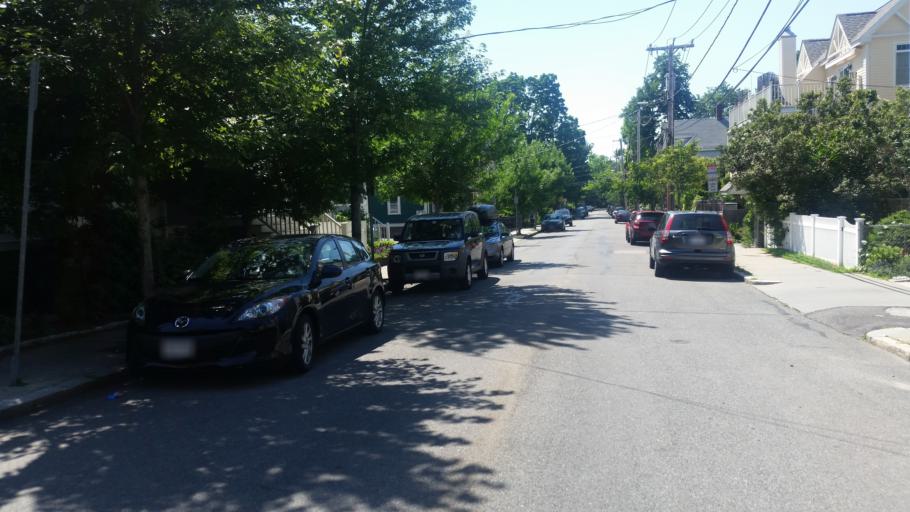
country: US
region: Massachusetts
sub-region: Middlesex County
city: Cambridge
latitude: 42.3890
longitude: -71.1255
